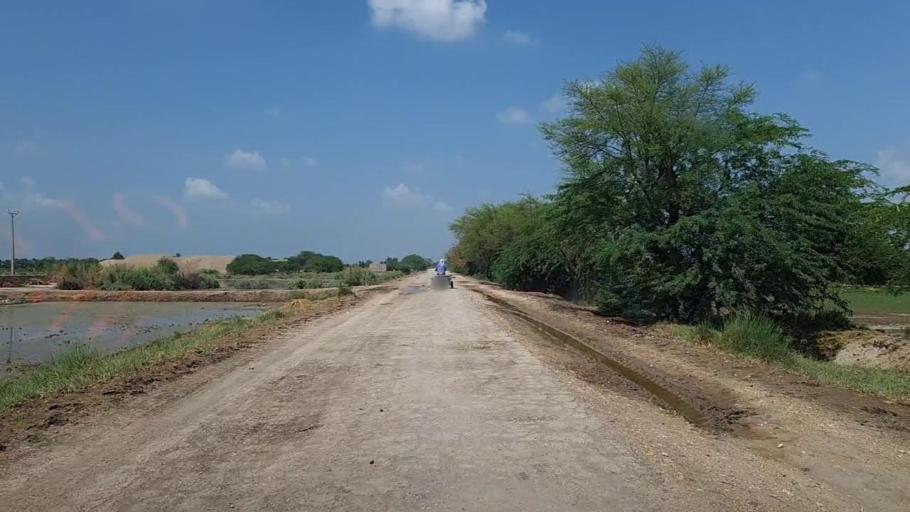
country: PK
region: Sindh
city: Kandiaro
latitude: 27.0099
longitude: 68.2627
